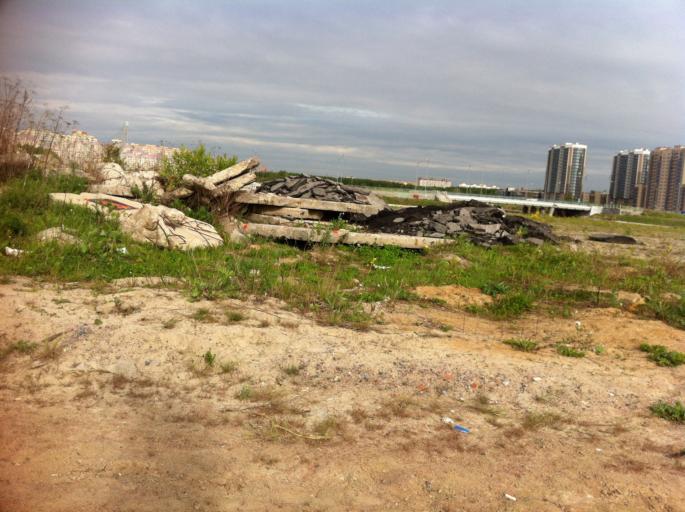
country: RU
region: St.-Petersburg
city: Sosnovaya Polyana
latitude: 59.8567
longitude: 30.1429
